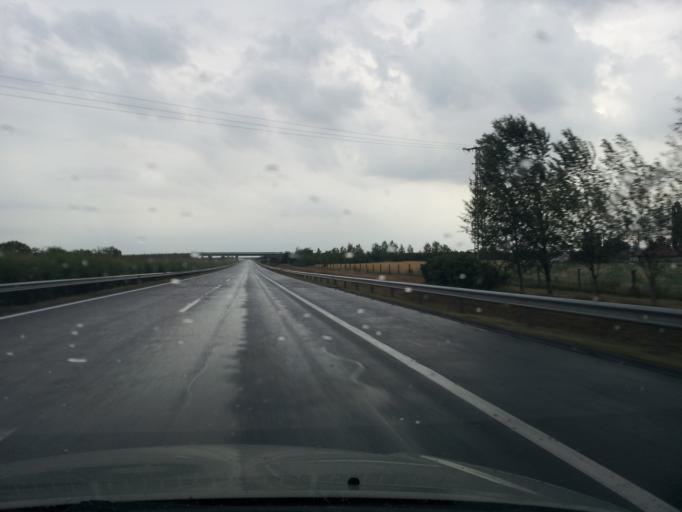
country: HU
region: Borsod-Abauj-Zemplen
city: Nyekladhaza
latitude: 47.9485
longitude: 20.8798
